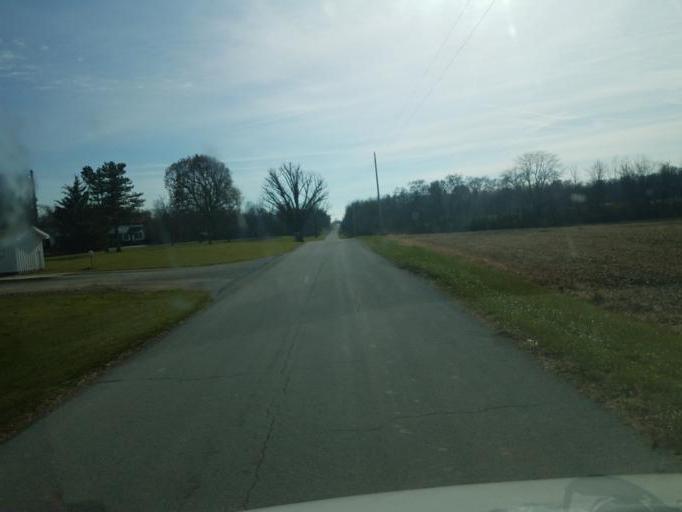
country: US
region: Ohio
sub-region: Hardin County
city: Forest
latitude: 40.6571
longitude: -83.4393
